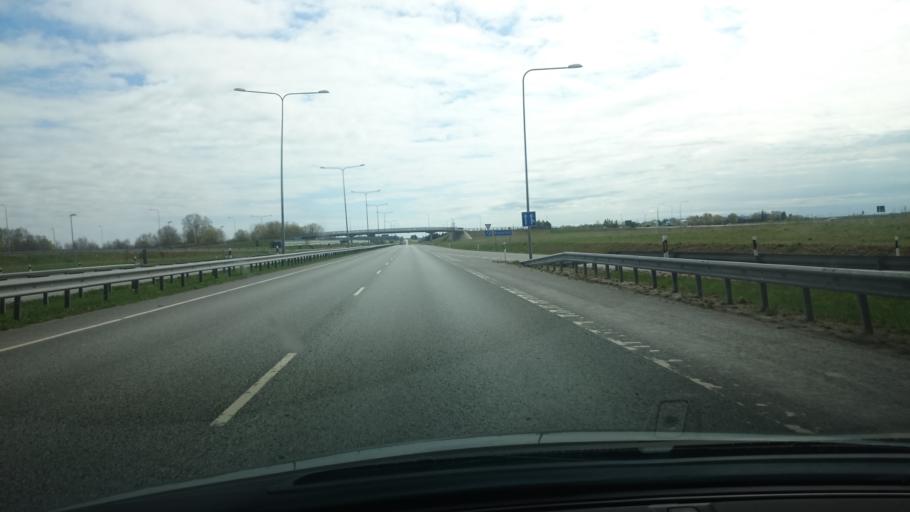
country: EE
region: Laeaene-Virumaa
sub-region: Haljala vald
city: Haljala
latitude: 59.4239
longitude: 26.2695
